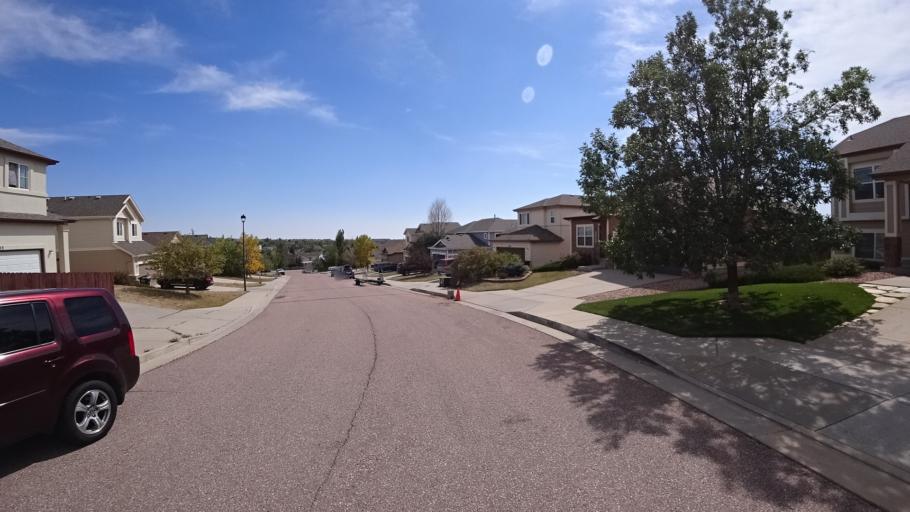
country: US
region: Colorado
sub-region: El Paso County
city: Cimarron Hills
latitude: 38.9085
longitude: -104.7092
